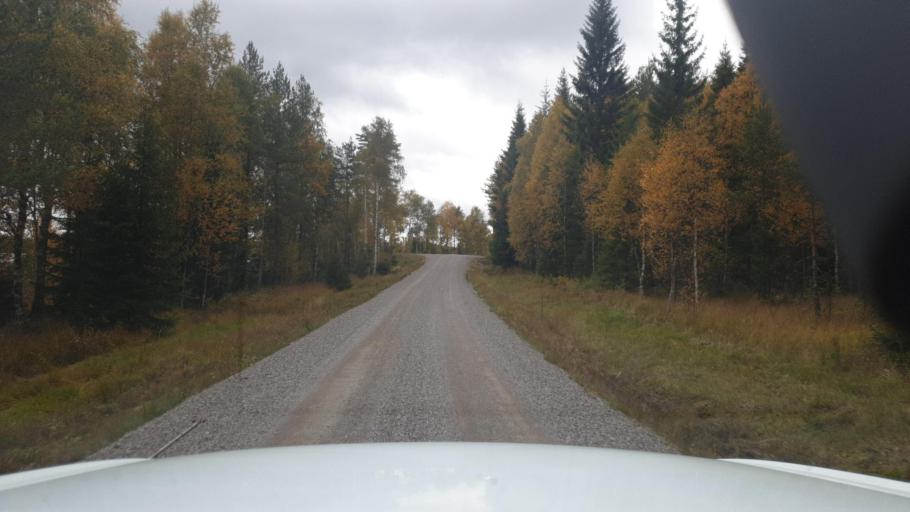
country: SE
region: Vaermland
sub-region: Eda Kommun
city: Charlottenberg
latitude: 60.1035
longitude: 12.6071
